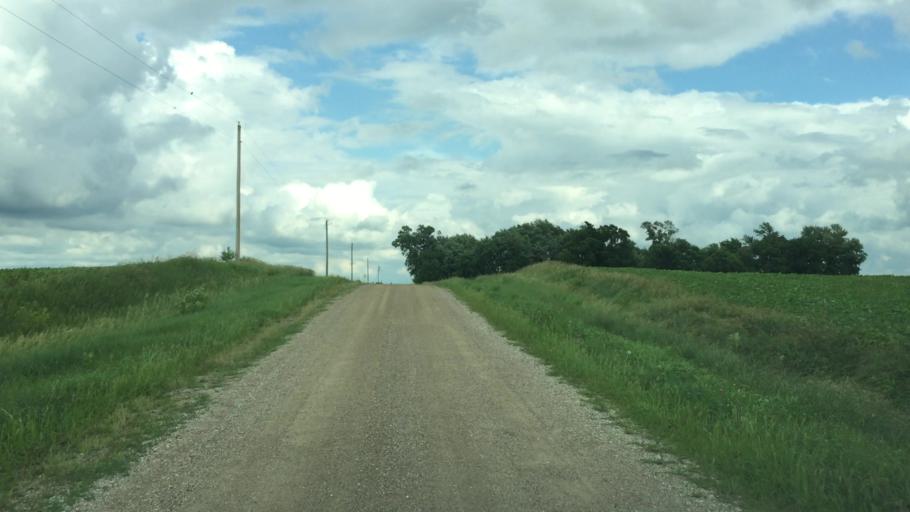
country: US
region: Iowa
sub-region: Jasper County
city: Newton
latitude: 41.7461
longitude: -93.0184
